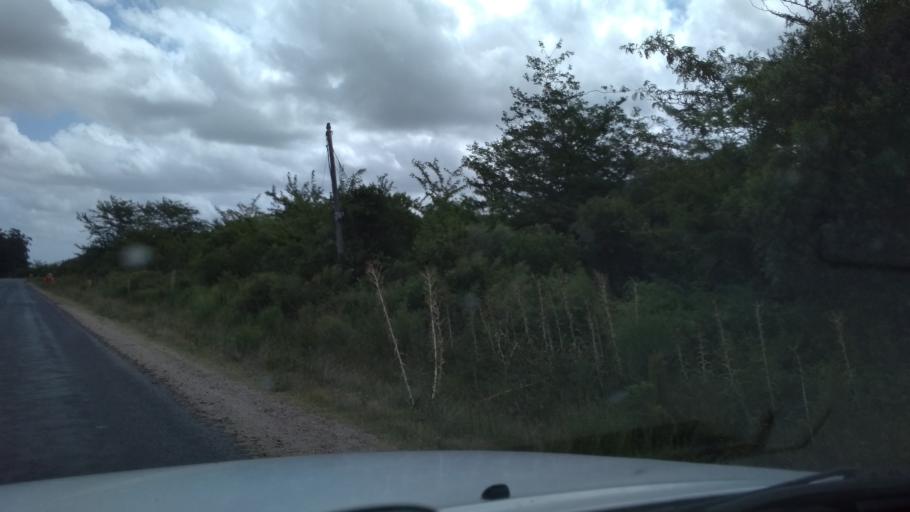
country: UY
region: Canelones
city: San Ramon
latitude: -34.2725
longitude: -55.9458
